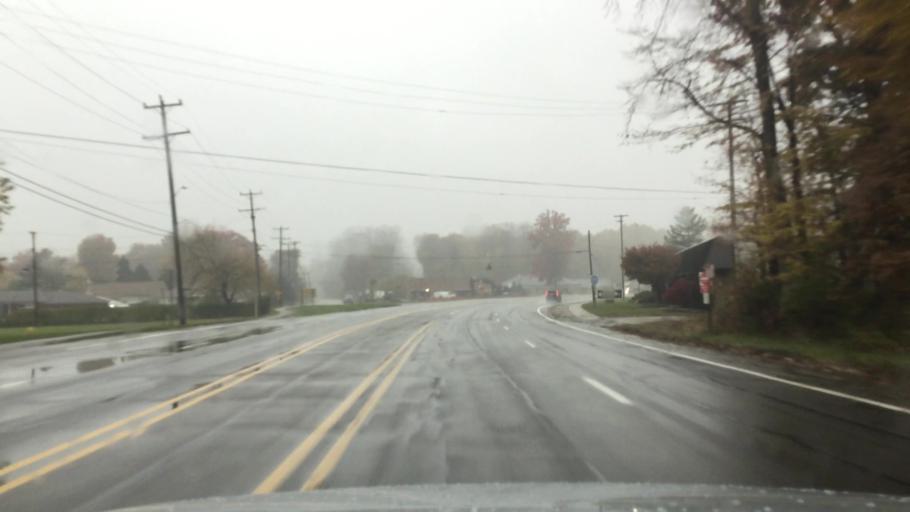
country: US
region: Michigan
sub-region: Macomb County
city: New Baltimore
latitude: 42.6867
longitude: -82.7183
